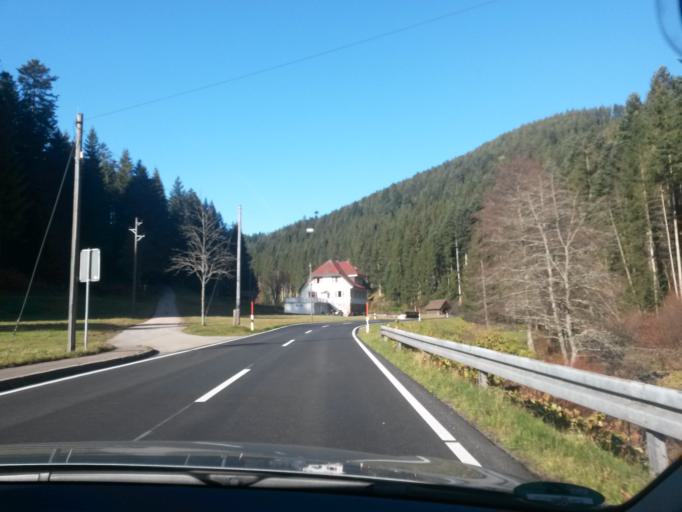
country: DE
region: Baden-Wuerttemberg
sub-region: Karlsruhe Region
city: Bad Rippoldsau-Schapbach
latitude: 48.4414
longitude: 8.3139
